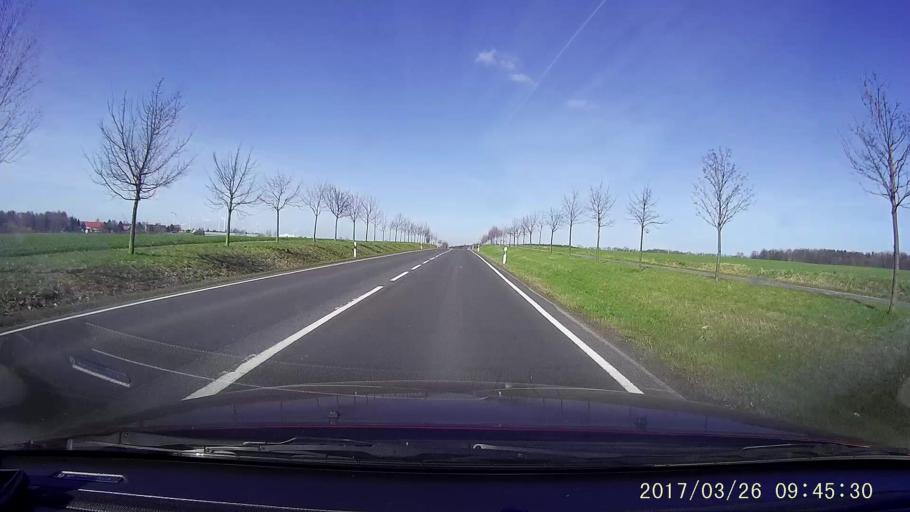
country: DE
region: Saxony
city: Reichenbach
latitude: 51.1489
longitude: 14.8049
